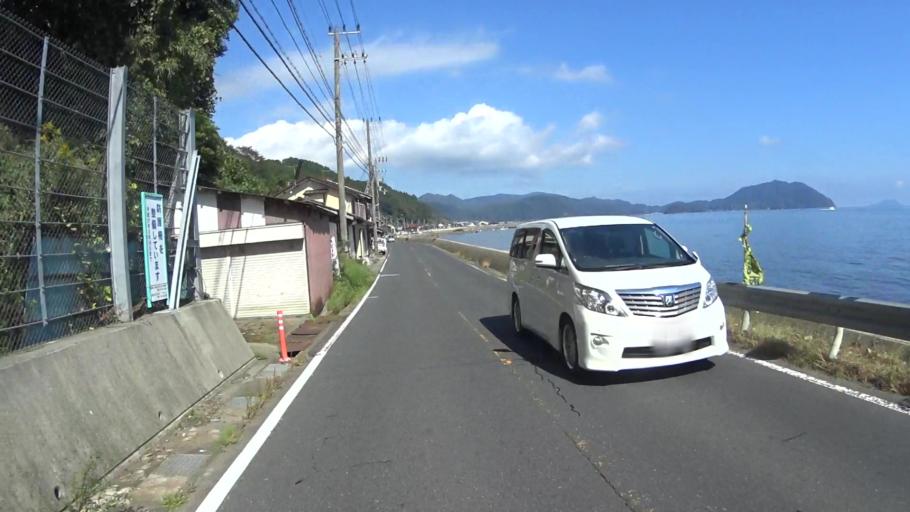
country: JP
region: Kyoto
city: Miyazu
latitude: 35.6458
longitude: 135.2513
